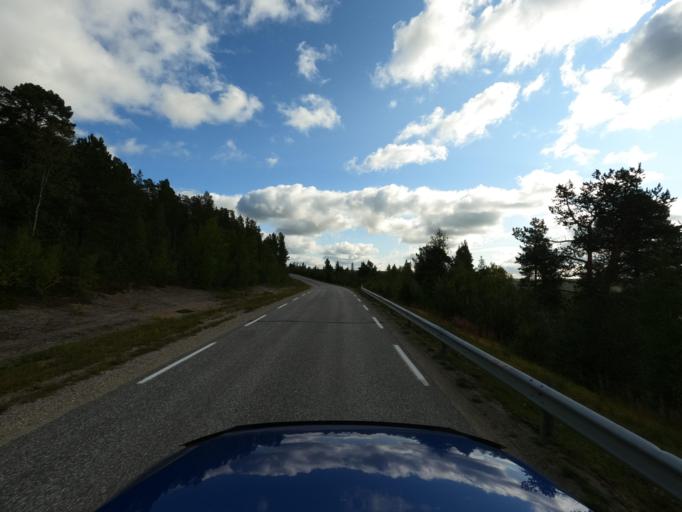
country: NO
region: Finnmark Fylke
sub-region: Karasjok
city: Karasjohka
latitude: 69.4428
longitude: 25.2525
